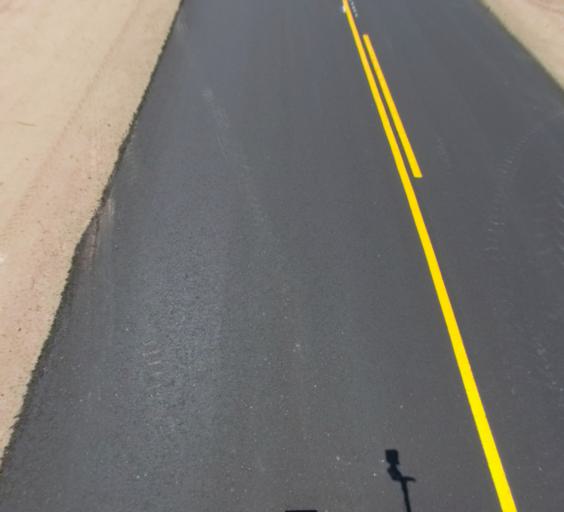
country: US
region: California
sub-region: Madera County
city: Bonadelle Ranchos-Madera Ranchos
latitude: 36.9011
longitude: -119.8576
